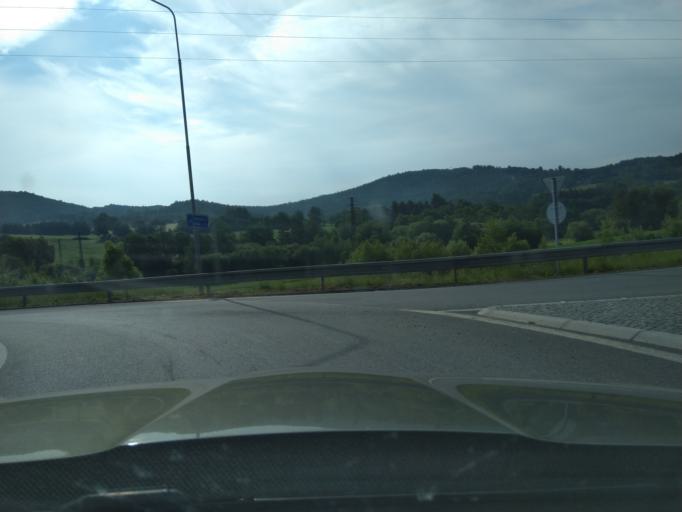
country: CZ
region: Jihocesky
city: Husinec
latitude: 49.0474
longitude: 14.0222
